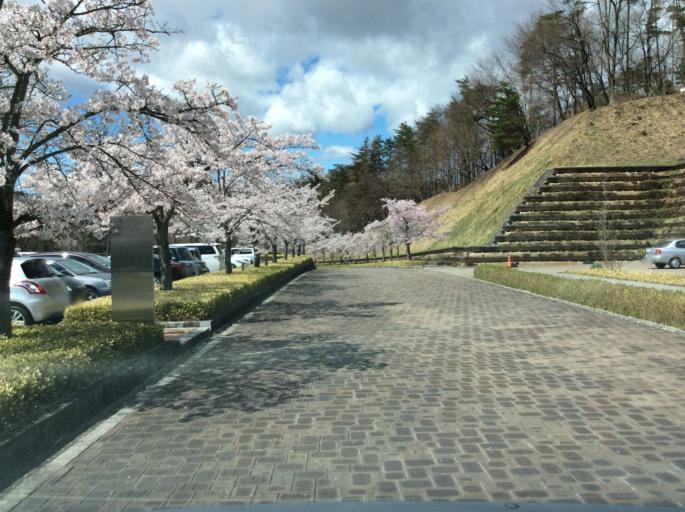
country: JP
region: Fukushima
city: Koriyama
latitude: 37.3523
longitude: 140.4289
